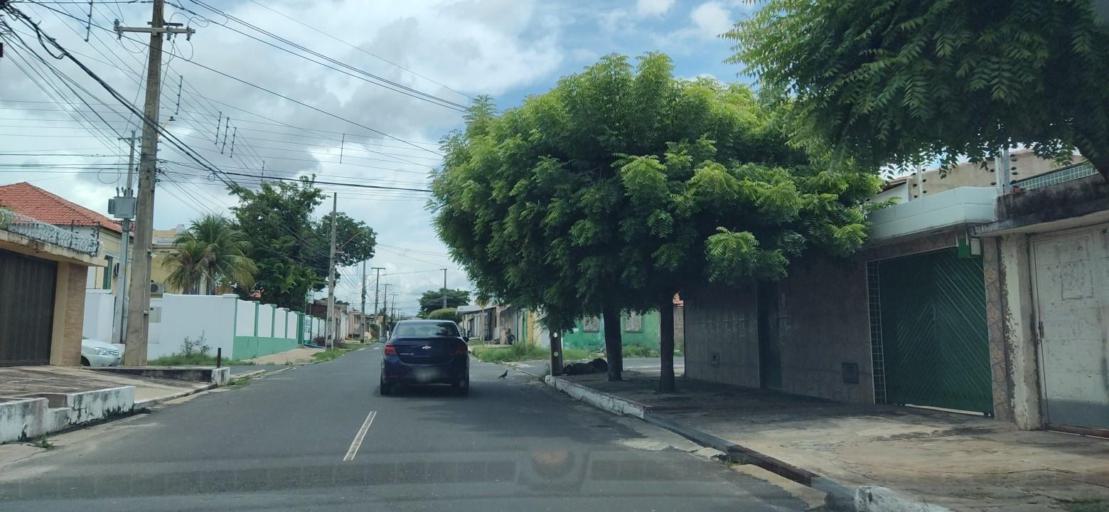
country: BR
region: Piaui
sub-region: Teresina
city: Teresina
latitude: -5.0766
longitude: -42.8057
